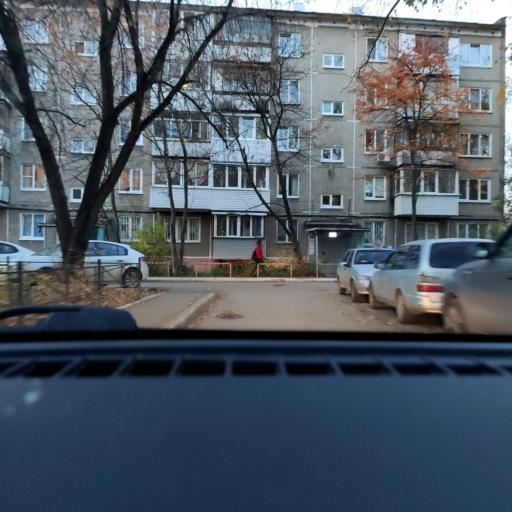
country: RU
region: Perm
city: Perm
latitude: 57.9808
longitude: 56.2208
